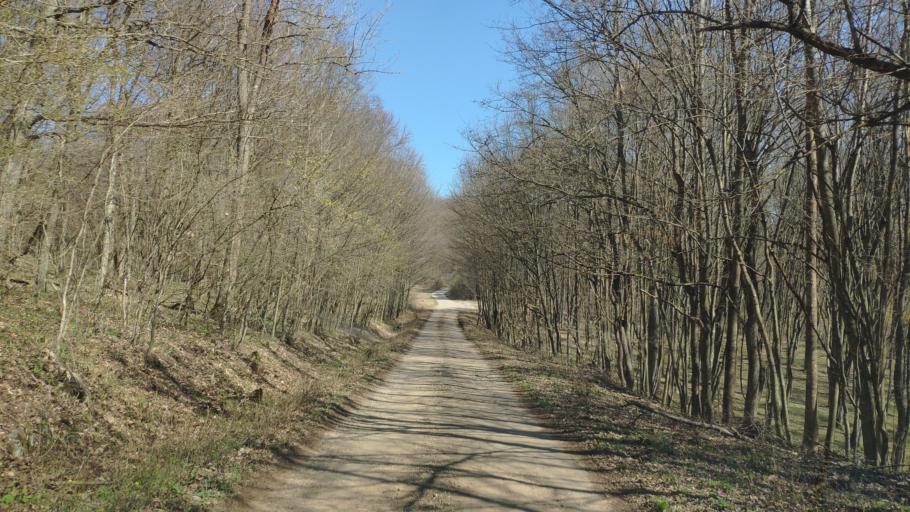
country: SK
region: Kosicky
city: Roznava
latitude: 48.5848
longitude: 20.4054
